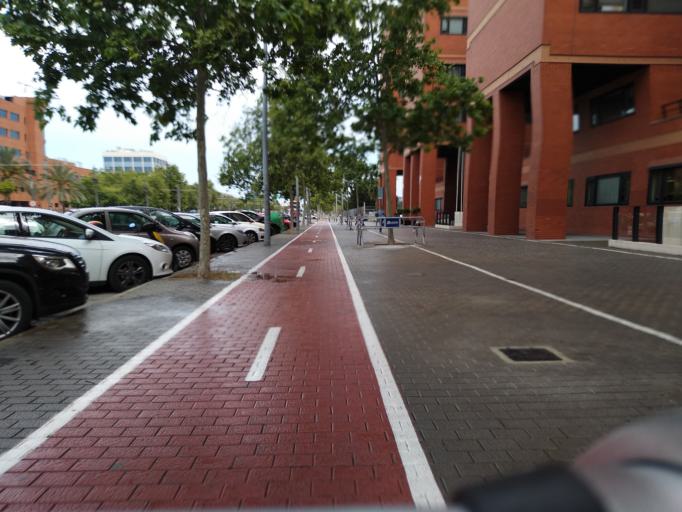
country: ES
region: Valencia
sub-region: Provincia de Valencia
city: Alboraya
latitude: 39.4785
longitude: -0.3415
